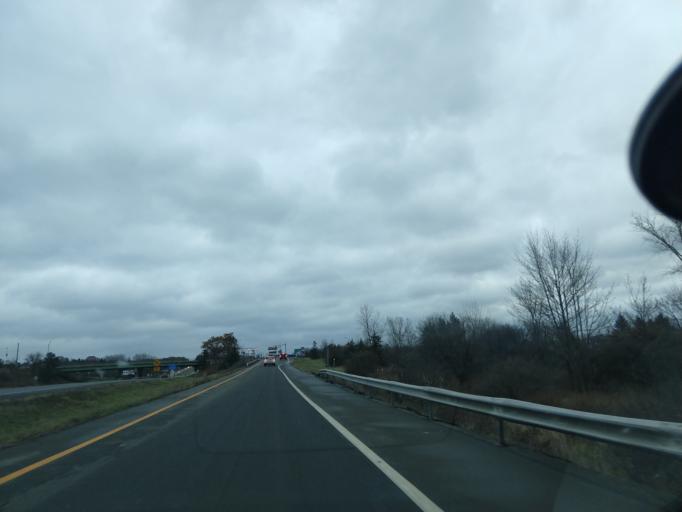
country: US
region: New York
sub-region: Tompkins County
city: Lansing
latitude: 42.4806
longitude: -76.4866
